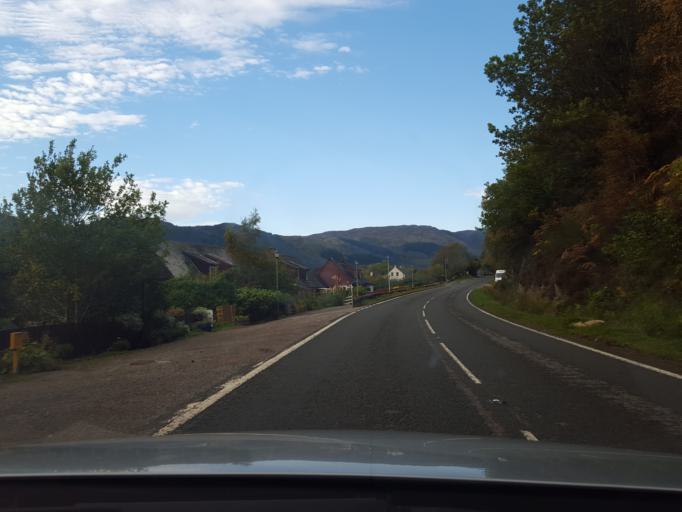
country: GB
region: Scotland
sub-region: Highland
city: Fort William
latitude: 57.2336
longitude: -5.4210
